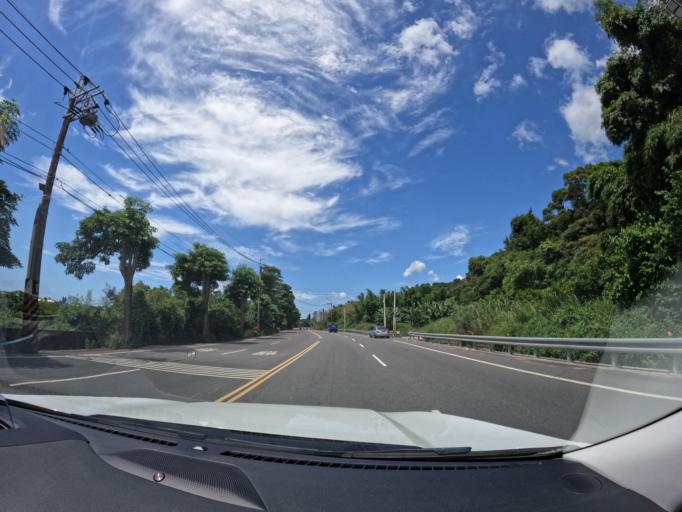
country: TW
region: Taipei
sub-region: Taipei
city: Banqiao
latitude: 25.1347
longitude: 121.3922
